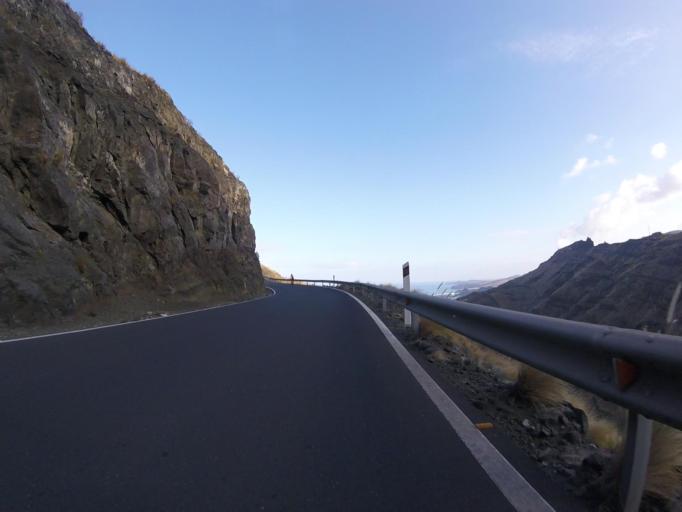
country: ES
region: Canary Islands
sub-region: Provincia de Las Palmas
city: Agaete
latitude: 28.0721
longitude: -15.7133
